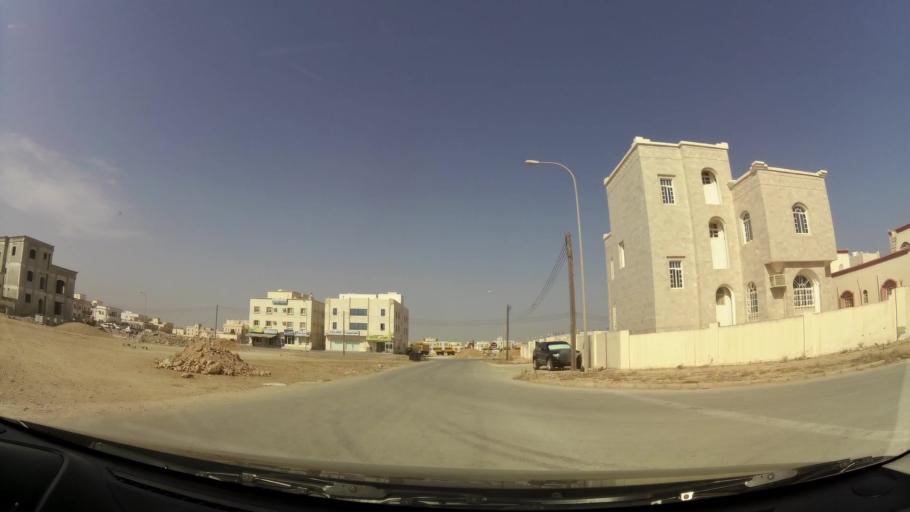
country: OM
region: Zufar
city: Salalah
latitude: 16.9995
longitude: 54.0107
